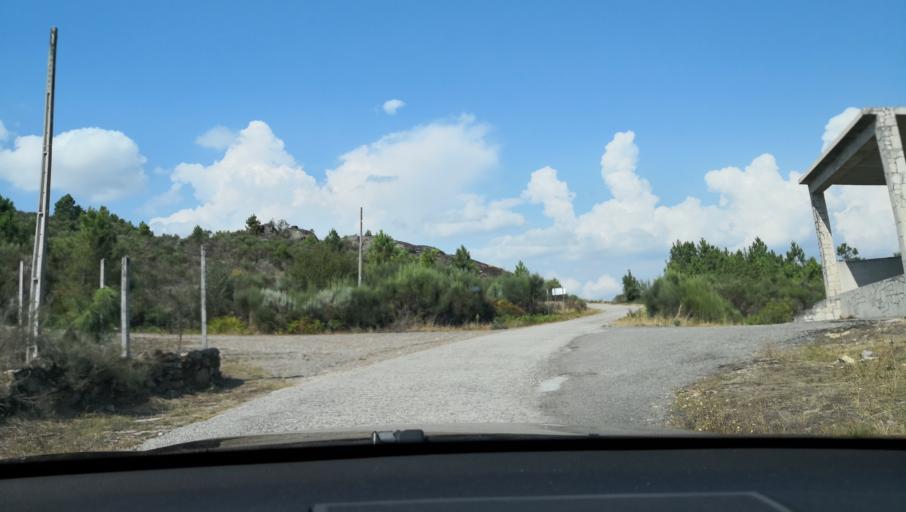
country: PT
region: Vila Real
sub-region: Sabrosa
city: Sabrosa
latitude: 41.3049
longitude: -7.5959
